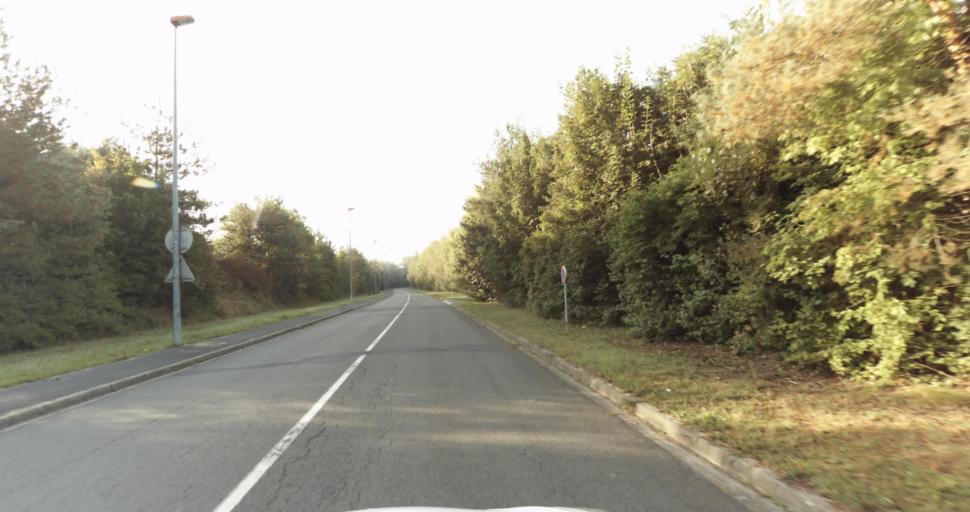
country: FR
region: Champagne-Ardenne
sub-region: Departement des Ardennes
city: Villers-Semeuse
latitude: 49.7308
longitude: 4.7571
